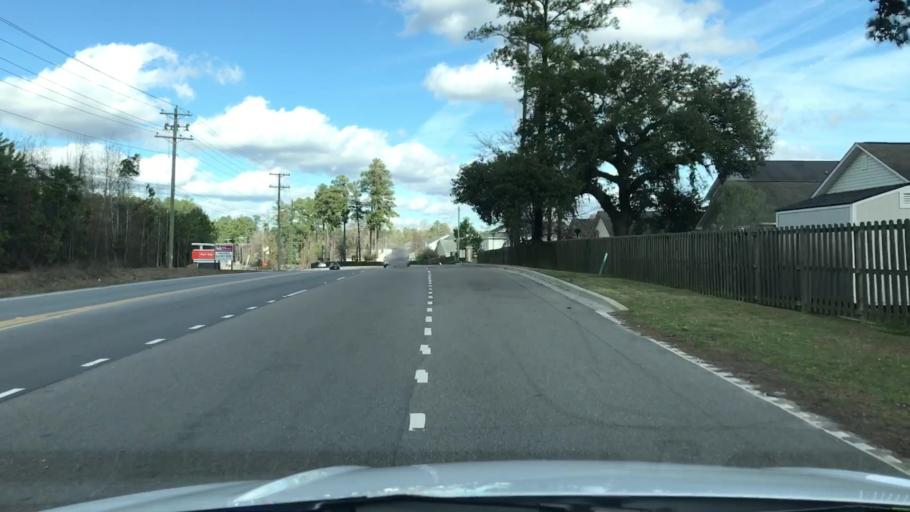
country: US
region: South Carolina
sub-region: Dorchester County
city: Summerville
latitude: 33.0891
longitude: -80.1993
